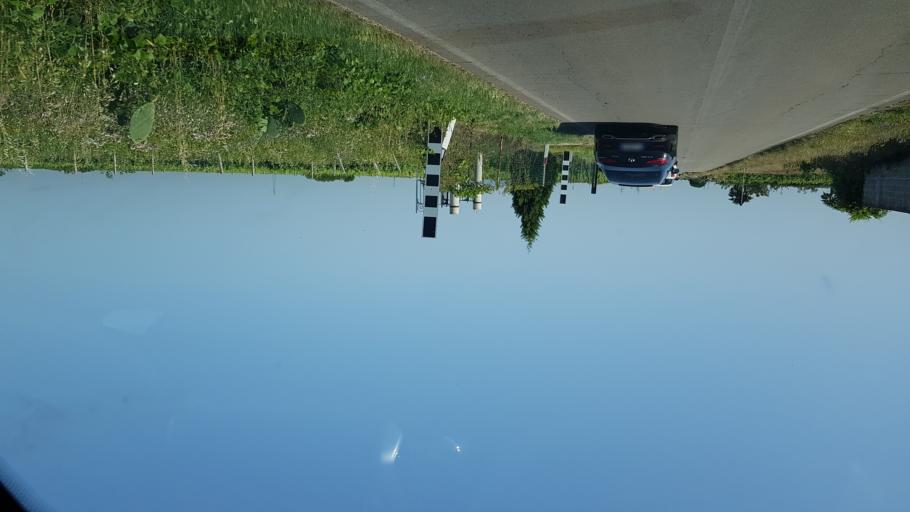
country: IT
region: Apulia
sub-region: Provincia di Brindisi
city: San Pancrazio Salentino
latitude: 40.4001
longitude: 17.8352
